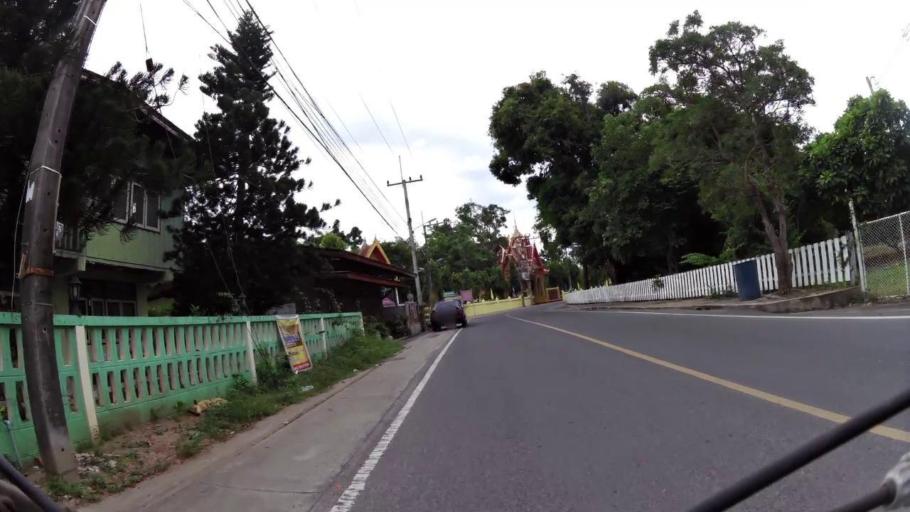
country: TH
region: Prachuap Khiri Khan
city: Prachuap Khiri Khan
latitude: 11.7502
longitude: 99.7898
